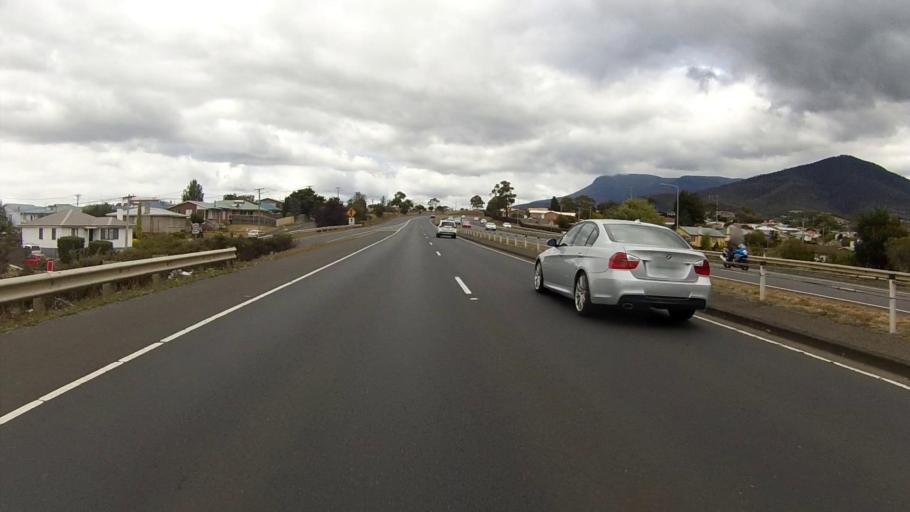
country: AU
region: Tasmania
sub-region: Glenorchy
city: Claremont
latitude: -42.7997
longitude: 147.2489
